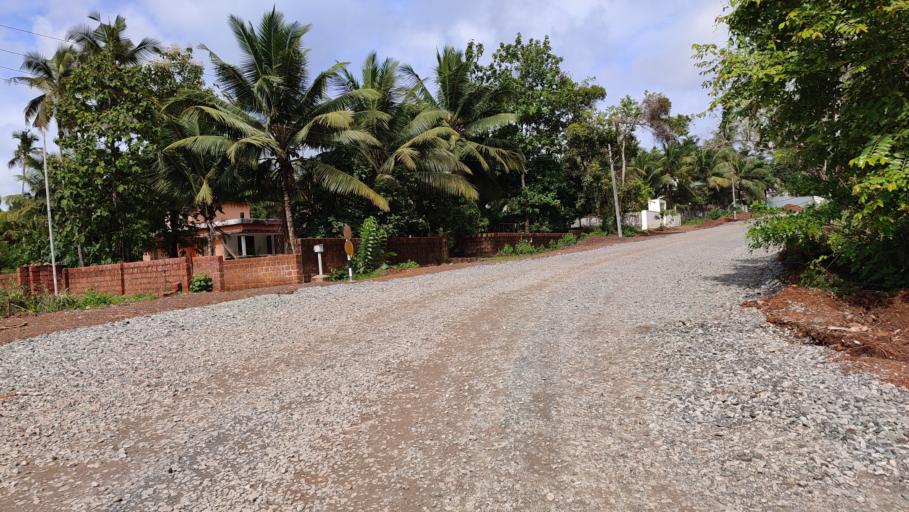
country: IN
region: Kerala
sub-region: Kasaragod District
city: Kasaragod
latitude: 12.5134
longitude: 75.0697
